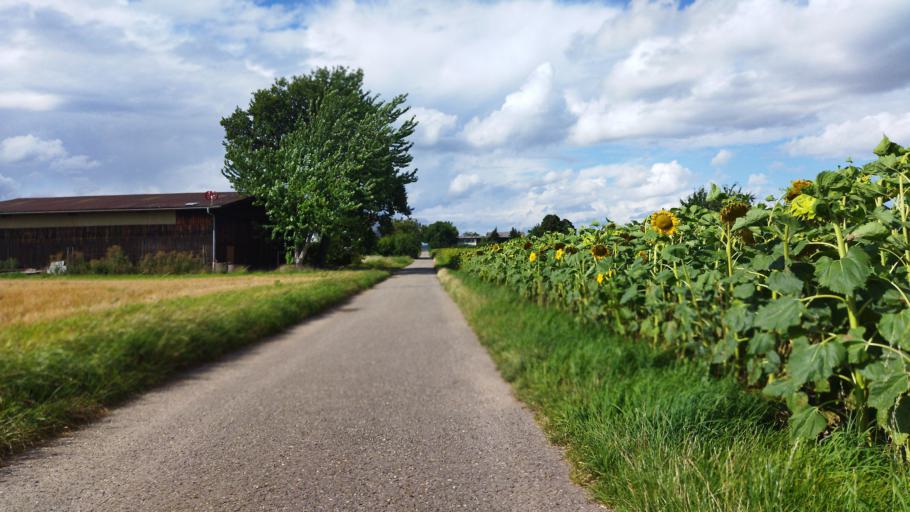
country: DE
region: Baden-Wuerttemberg
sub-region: Regierungsbezirk Stuttgart
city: Bonnigheim
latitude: 49.0444
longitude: 9.0865
